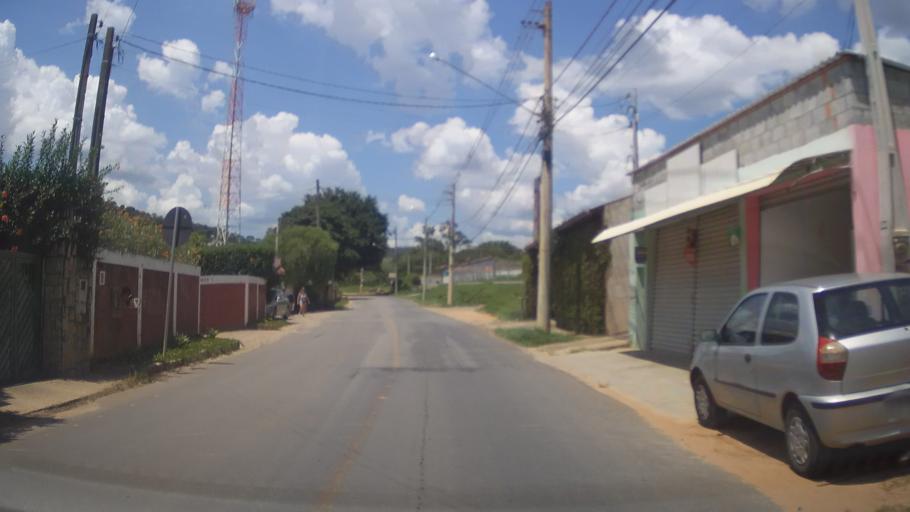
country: BR
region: Sao Paulo
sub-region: Campo Limpo Paulista
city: Campo Limpo Paulista
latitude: -23.1317
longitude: -46.8109
